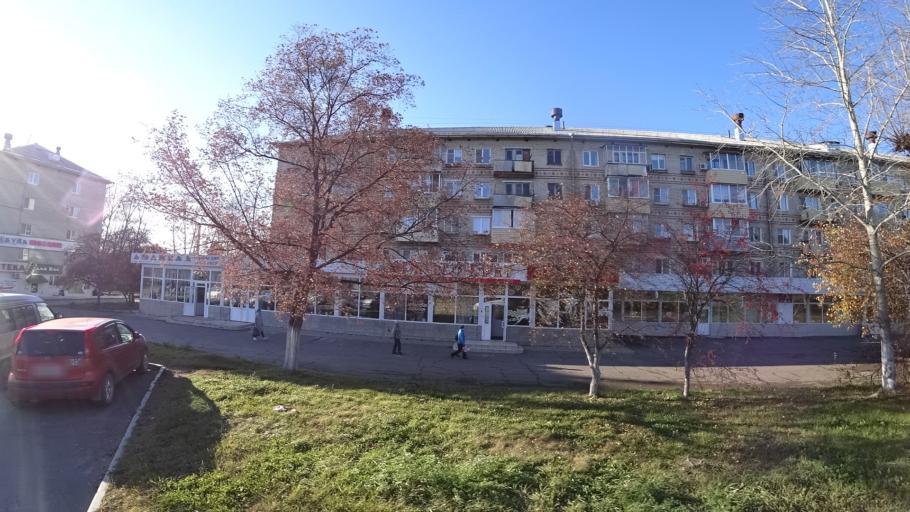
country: RU
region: Khabarovsk Krai
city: Amursk
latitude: 50.2259
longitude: 136.9086
